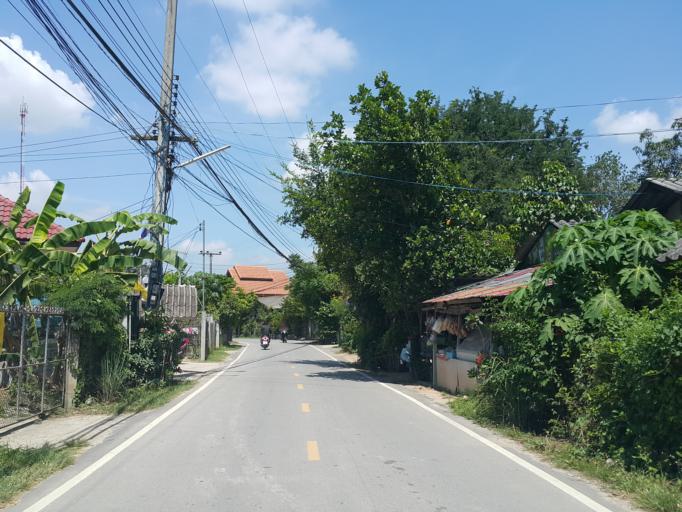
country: TH
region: Chiang Mai
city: San Sai
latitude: 18.8038
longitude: 99.0663
